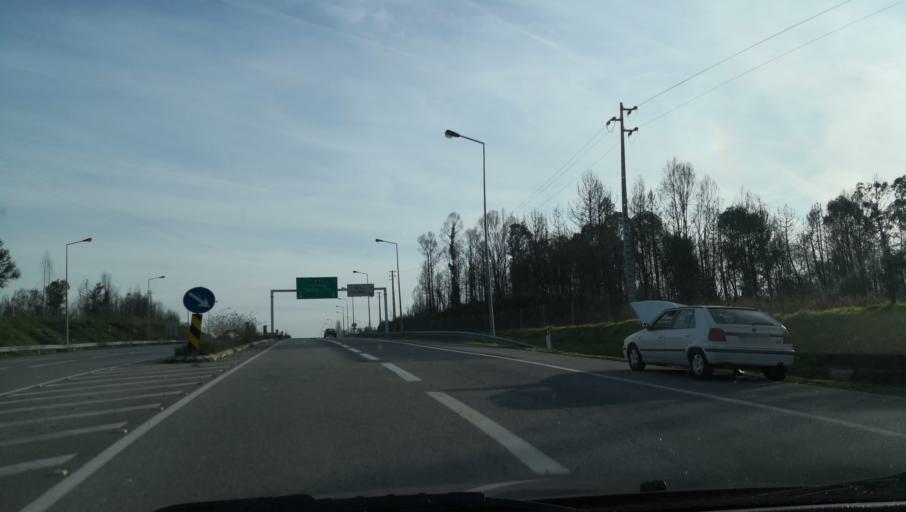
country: PT
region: Viseu
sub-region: Concelho de Tondela
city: Tondela
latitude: 40.5039
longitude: -8.0840
